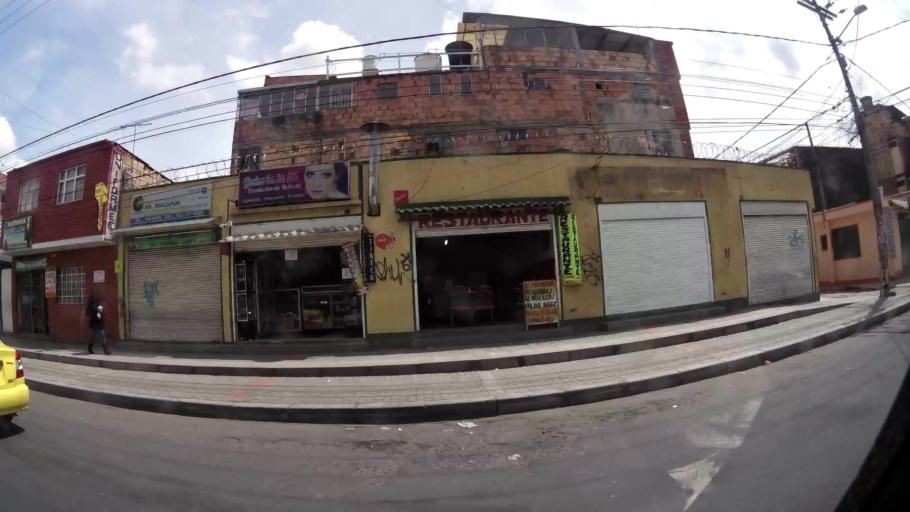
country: CO
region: Bogota D.C.
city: Barrio San Luis
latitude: 4.7027
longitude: -74.1090
